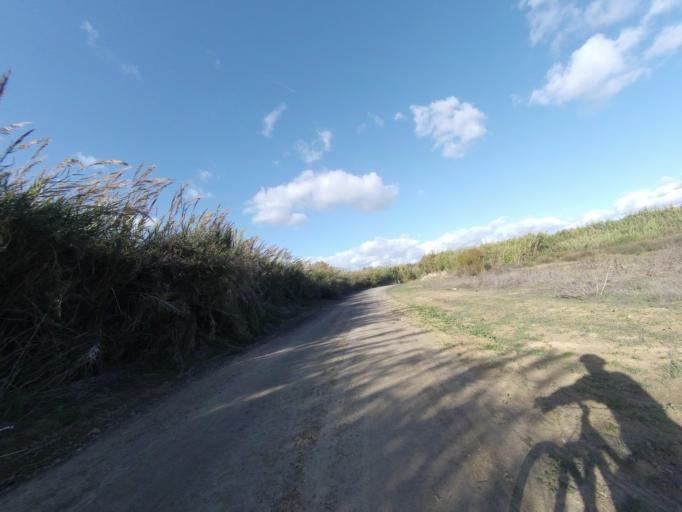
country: ES
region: Andalusia
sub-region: Provincia de Huelva
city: Palos de la Frontera
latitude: 37.2560
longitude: -6.8761
